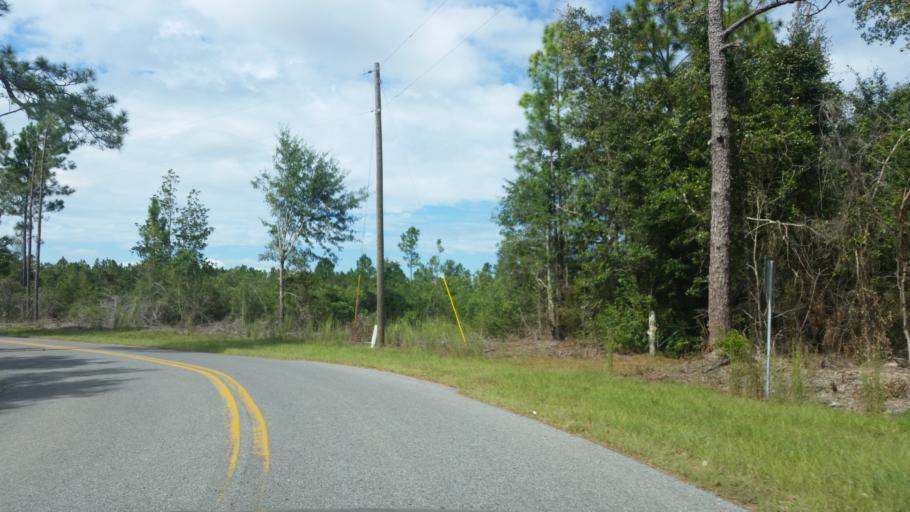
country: US
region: Florida
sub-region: Santa Rosa County
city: Point Baker
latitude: 30.7361
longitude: -87.0135
